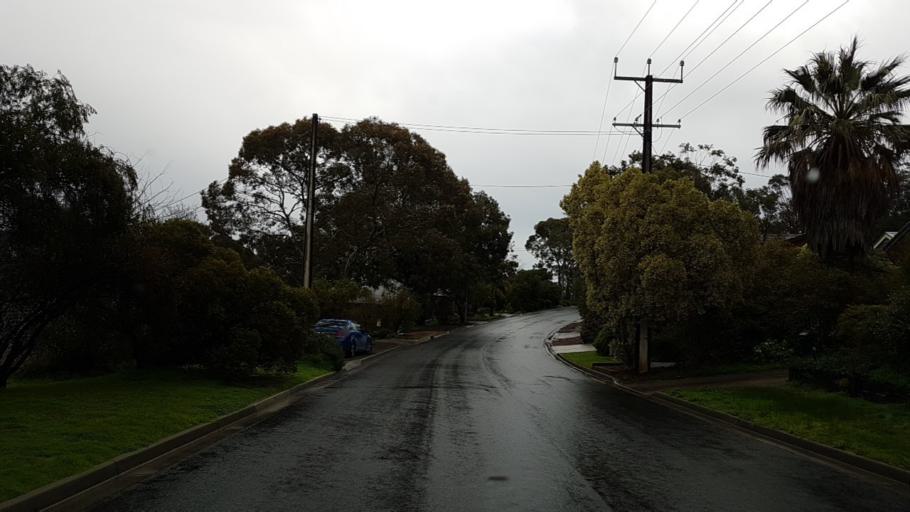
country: AU
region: South Australia
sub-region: Onkaparinga
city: Bedford Park
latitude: -35.0430
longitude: 138.5808
